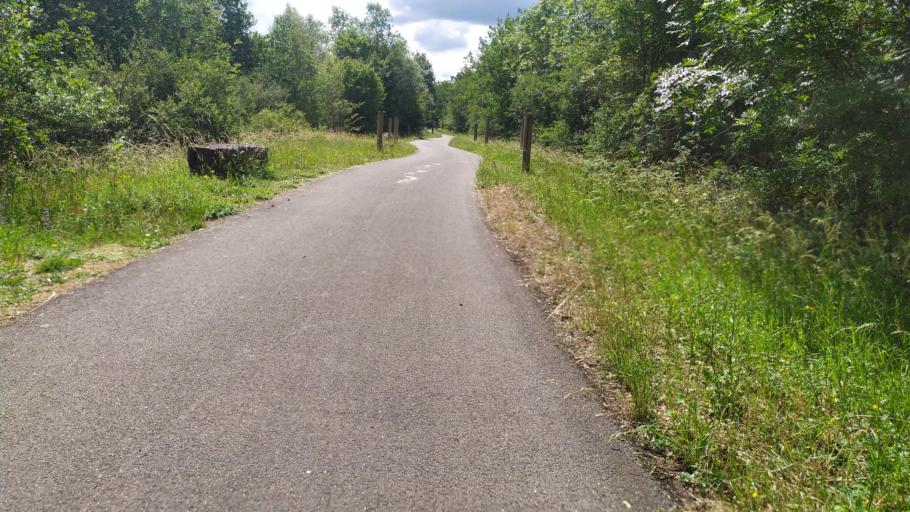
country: BE
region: Wallonia
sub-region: Province de Namur
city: Houyet
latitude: 50.1663
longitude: 5.0540
